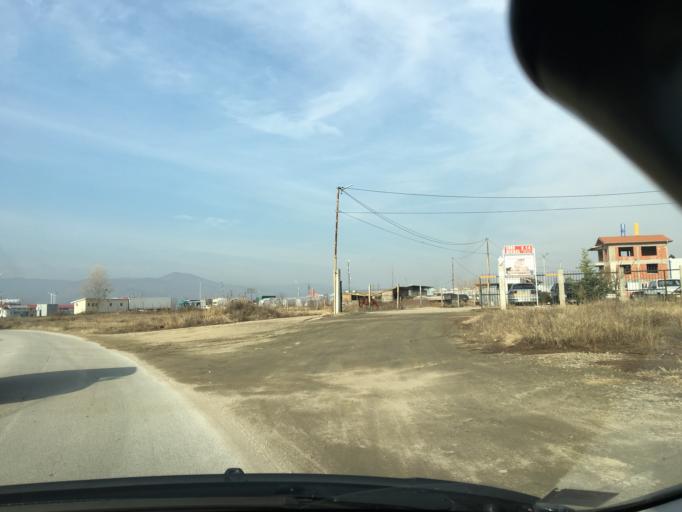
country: BG
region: Blagoevgrad
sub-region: Obshtina Sandanski
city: Sandanski
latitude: 41.5064
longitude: 23.2792
